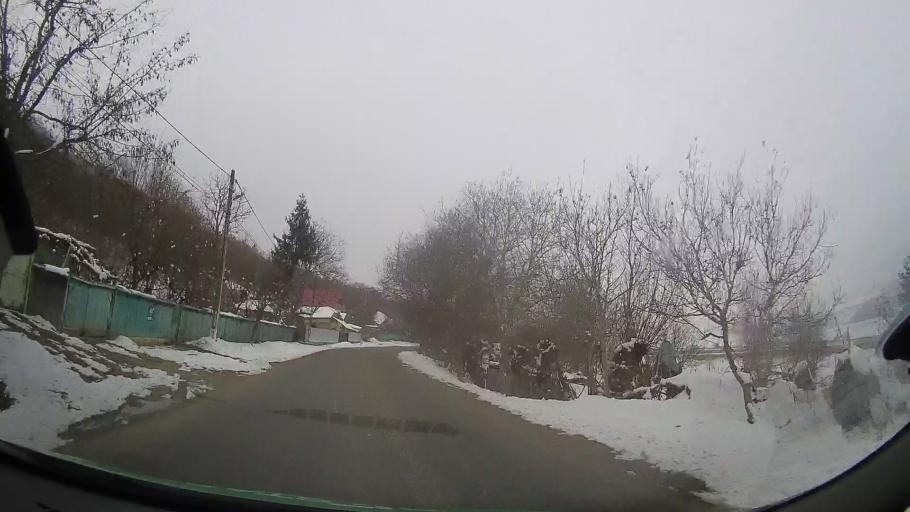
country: RO
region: Bacau
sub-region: Comuna Vultureni
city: Vultureni
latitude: 46.3456
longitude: 27.2903
